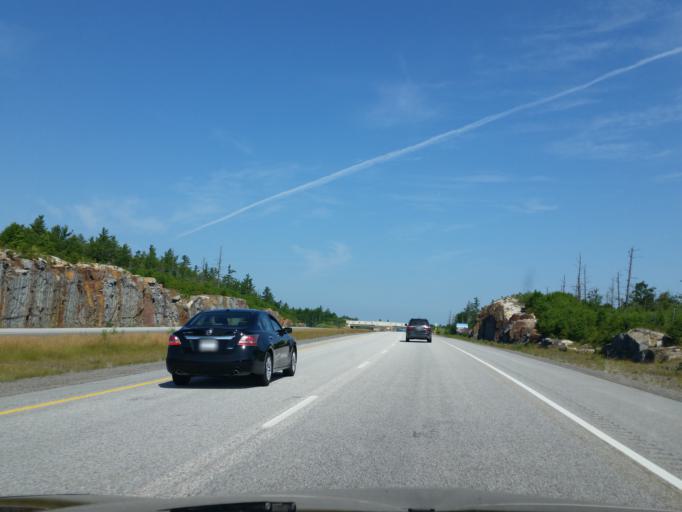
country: CA
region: Ontario
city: Greater Sudbury
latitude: 46.2334
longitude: -80.7770
